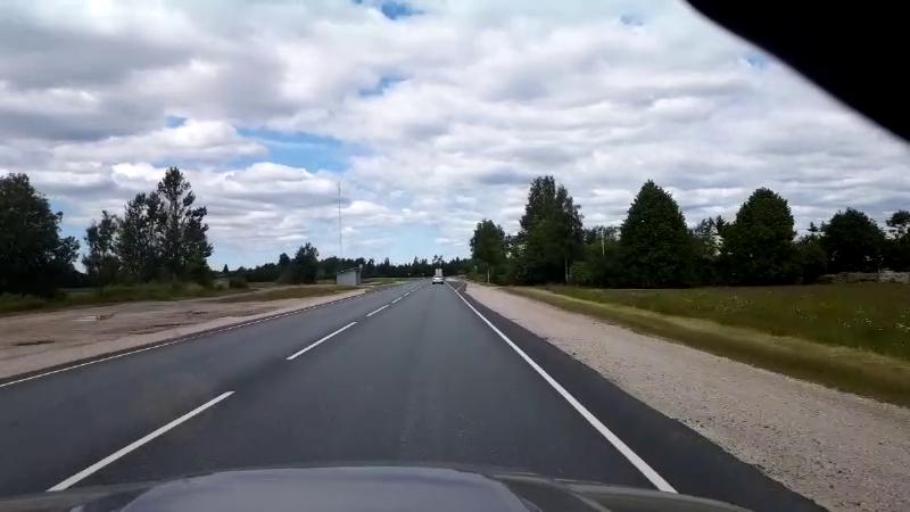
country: EE
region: Raplamaa
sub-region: Maerjamaa vald
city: Marjamaa
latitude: 58.7734
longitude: 24.4145
